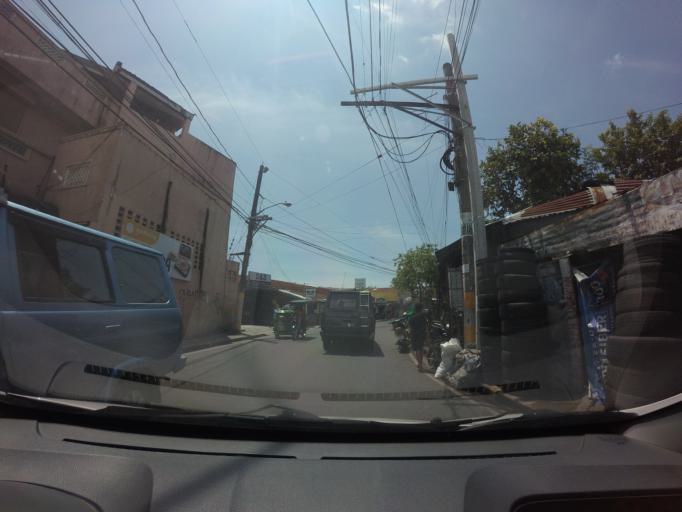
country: PH
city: Sambayanihan People's Village
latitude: 14.4283
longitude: 121.0131
